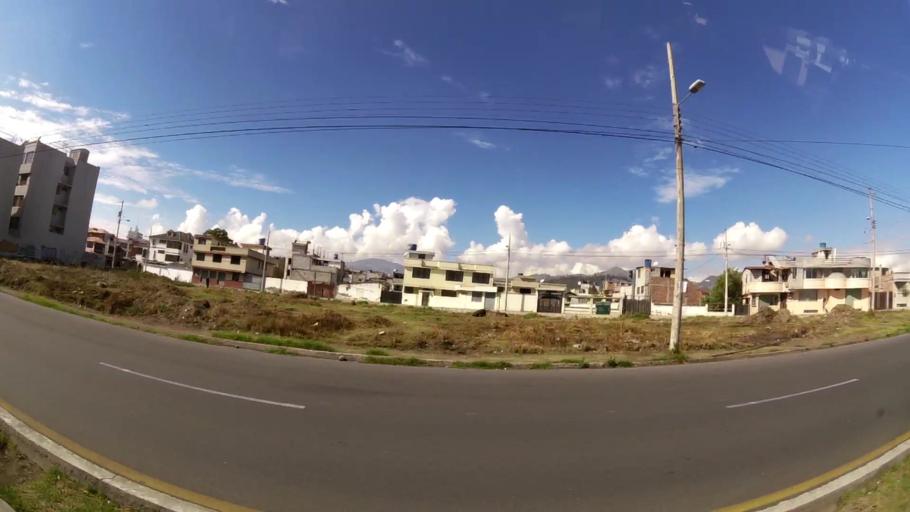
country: EC
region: Chimborazo
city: Riobamba
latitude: -1.6631
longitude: -78.6666
